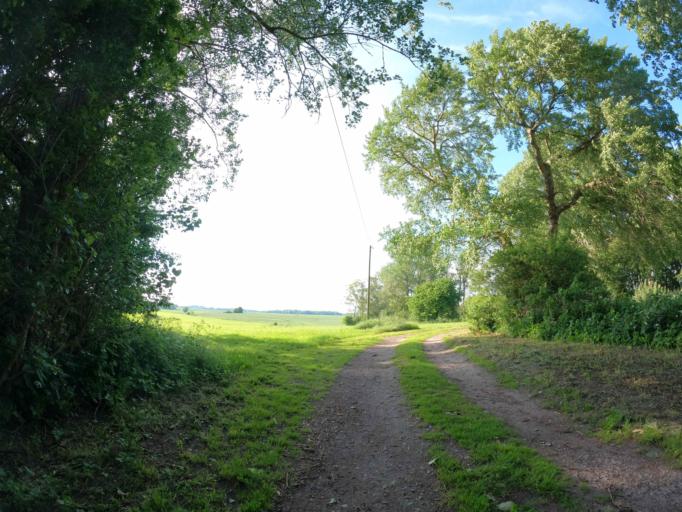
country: DE
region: Mecklenburg-Vorpommern
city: Altenpleen
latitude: 54.3321
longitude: 12.9680
